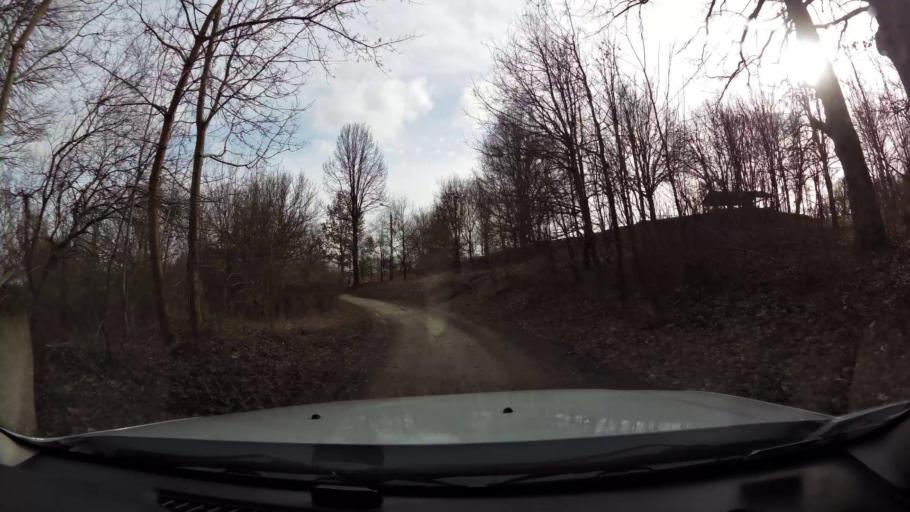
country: PL
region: West Pomeranian Voivodeship
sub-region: Powiat drawski
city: Drawsko Pomorskie
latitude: 53.5148
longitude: 15.7496
